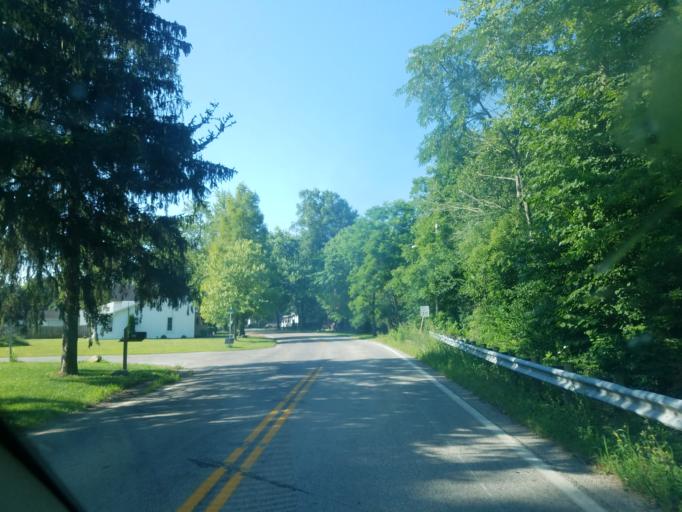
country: US
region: Ohio
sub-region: Marion County
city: Prospect
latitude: 40.4558
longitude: -83.1898
